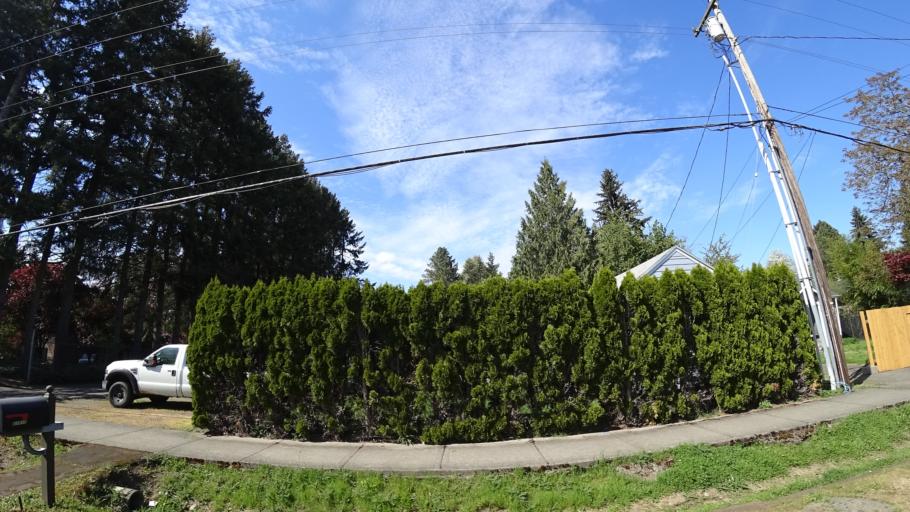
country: US
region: Oregon
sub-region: Washington County
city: Aloha
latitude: 45.4983
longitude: -122.8925
